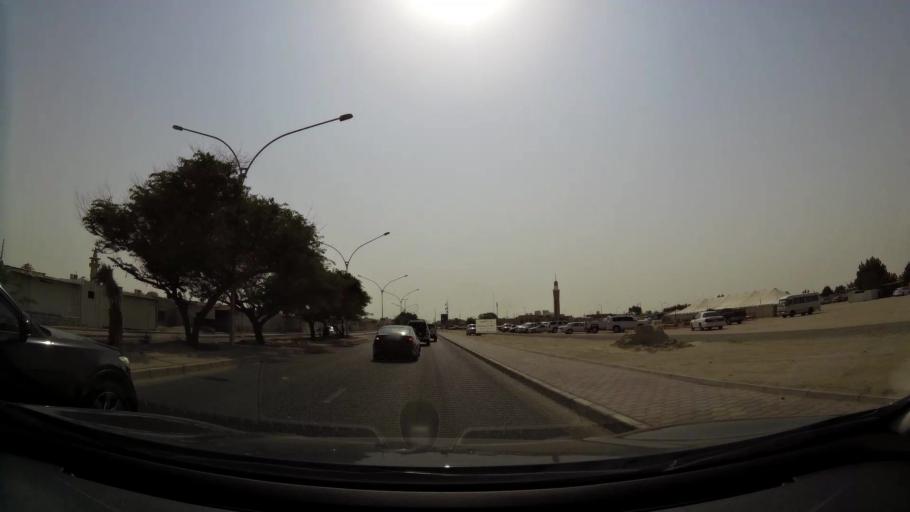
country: KW
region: Muhafazat al Jahra'
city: Al Jahra'
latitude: 29.3319
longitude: 47.6825
